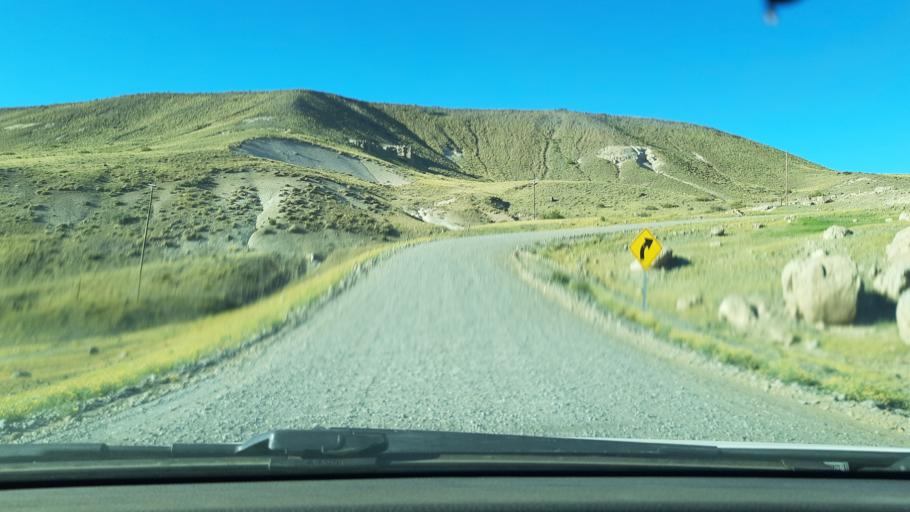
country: AR
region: Neuquen
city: Las Ovejas
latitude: -36.8229
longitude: -70.7071
